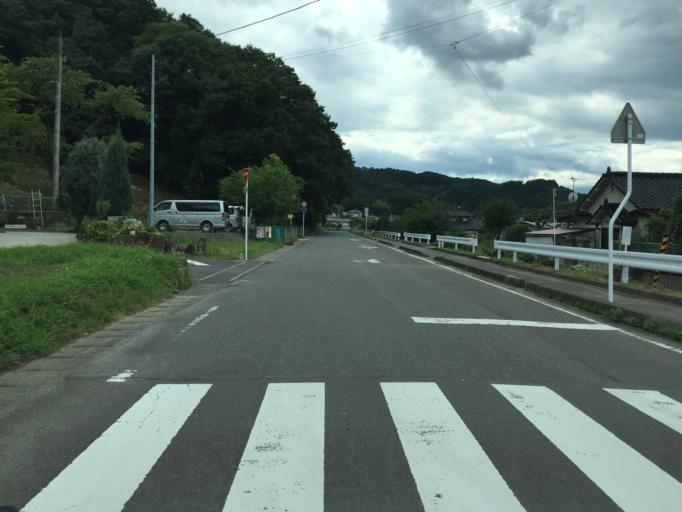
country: JP
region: Fukushima
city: Fukushima-shi
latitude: 37.7467
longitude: 140.4874
